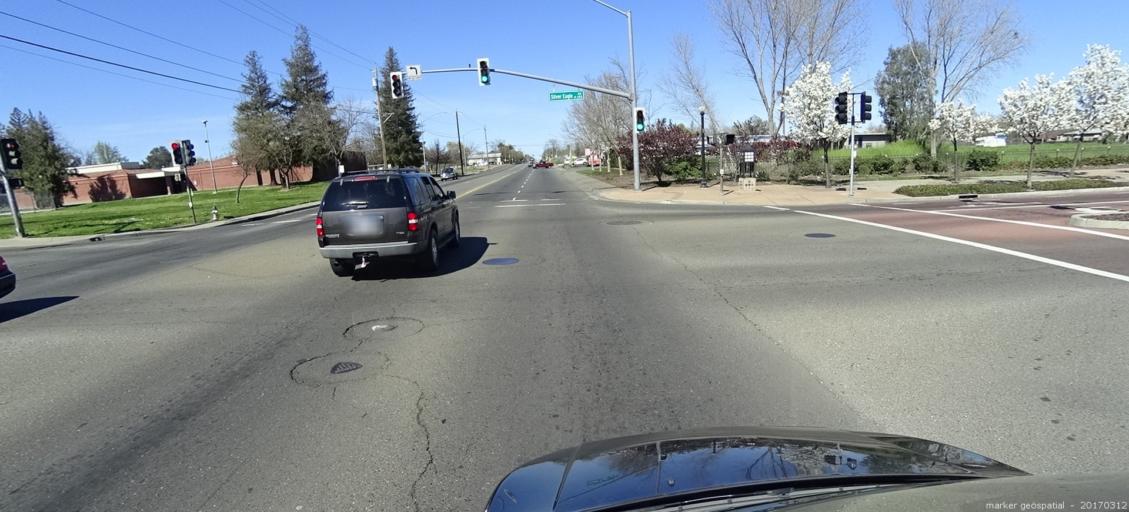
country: US
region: California
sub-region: Sacramento County
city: Sacramento
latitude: 38.6301
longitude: -121.4569
